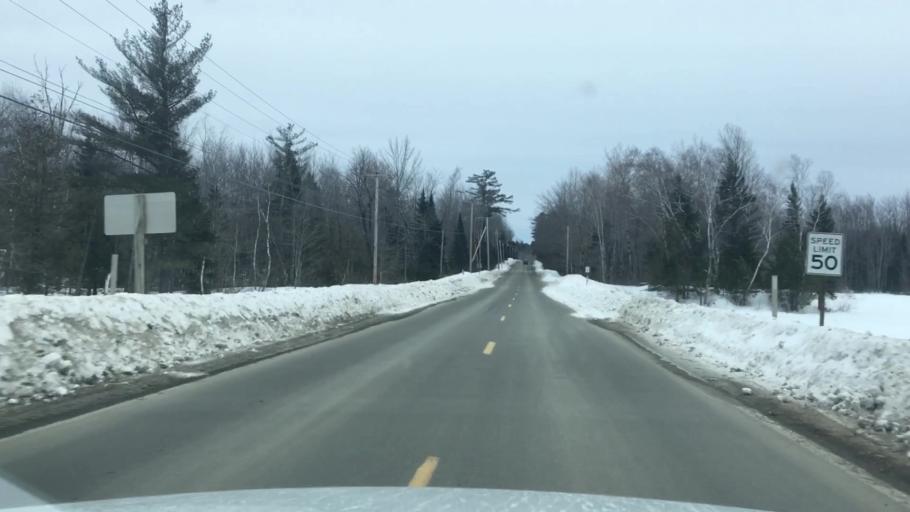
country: US
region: Maine
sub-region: Penobscot County
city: Charleston
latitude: 45.0518
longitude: -69.0302
